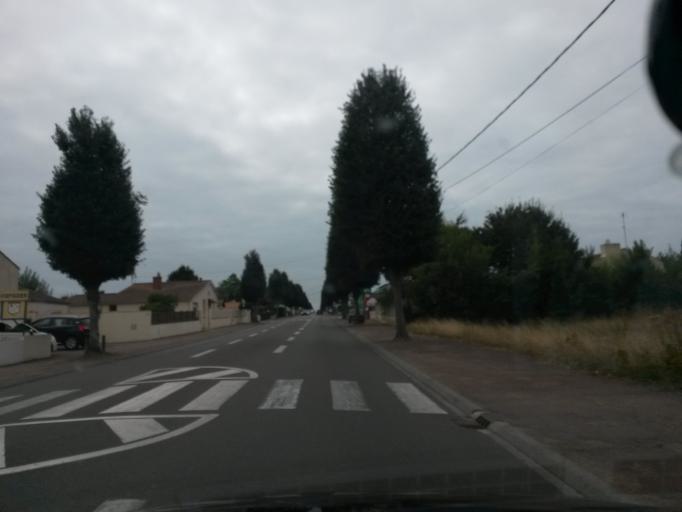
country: FR
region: Pays de la Loire
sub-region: Departement de la Vendee
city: Olonne-sur-Mer
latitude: 46.5308
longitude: -1.7742
